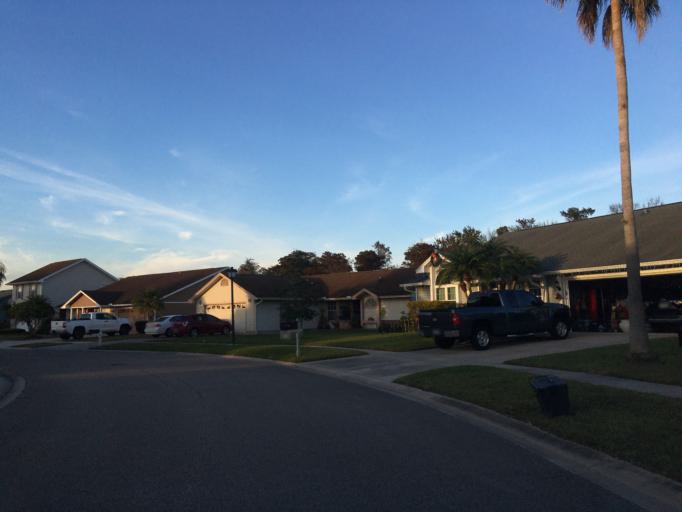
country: US
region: Florida
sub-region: Orange County
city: Azalea Park
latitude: 28.5169
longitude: -81.2745
